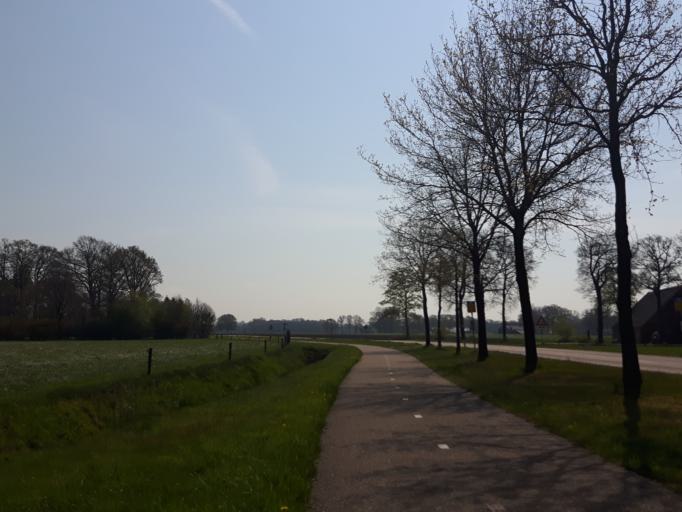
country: NL
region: Overijssel
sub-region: Gemeente Haaksbergen
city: Haaksbergen
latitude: 52.1443
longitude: 6.8107
